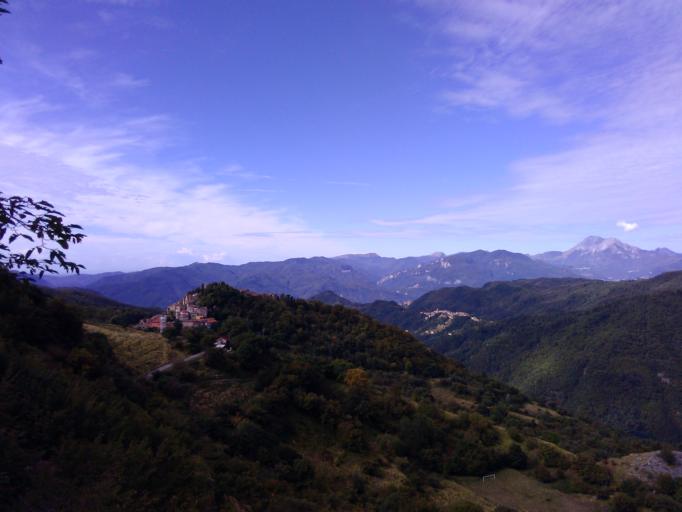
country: IT
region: Tuscany
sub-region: Provincia di Lucca
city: Coreglia Antelminelli
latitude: 44.0663
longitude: 10.5987
